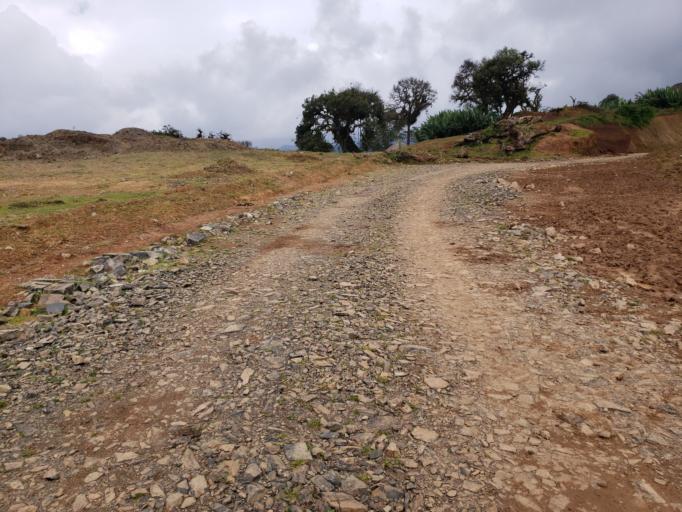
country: ET
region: Oromiya
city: Dodola
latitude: 6.6514
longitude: 39.3615
